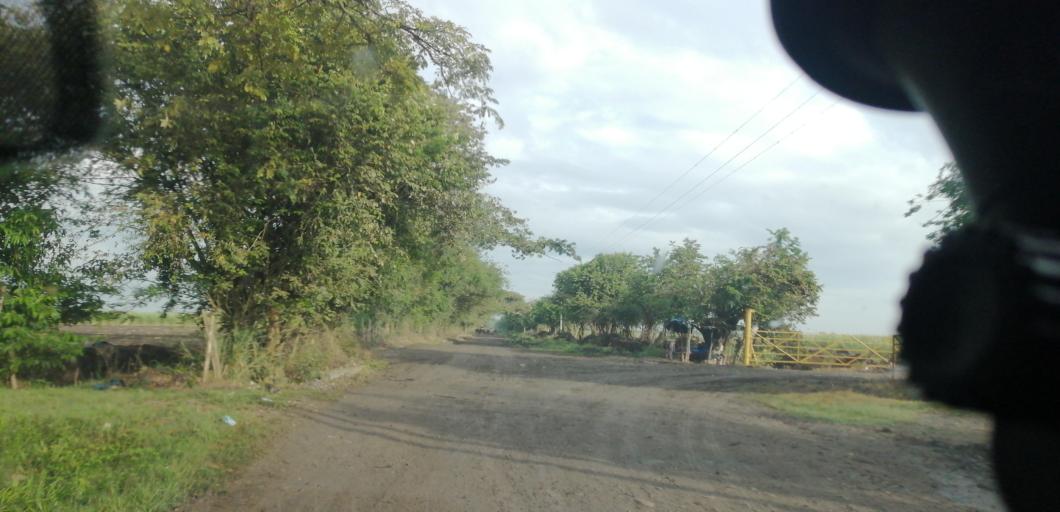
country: CO
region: Valle del Cauca
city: Palmira
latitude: 3.5435
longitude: -76.3608
